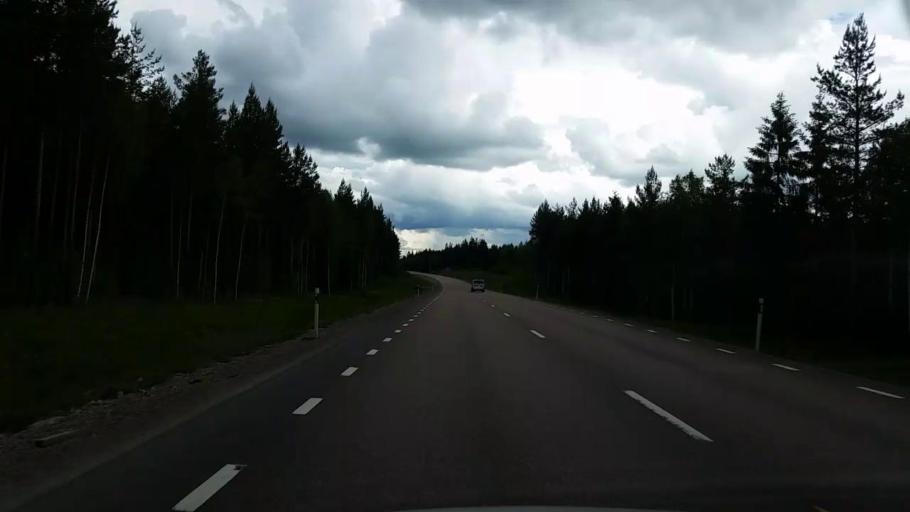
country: SE
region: Dalarna
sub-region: Avesta Kommun
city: Horndal
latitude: 60.4657
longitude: 16.4478
